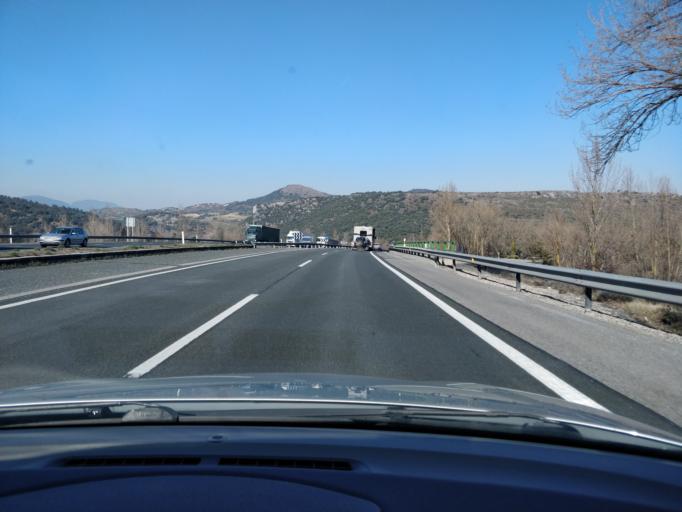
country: ES
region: Castille and Leon
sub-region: Provincia de Burgos
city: Ameyugo
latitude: 42.6475
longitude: -3.0813
